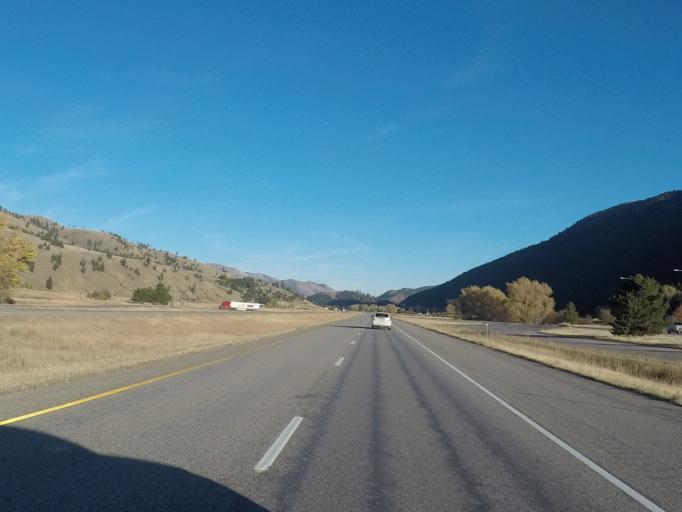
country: US
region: Montana
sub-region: Missoula County
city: Clinton
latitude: 46.7269
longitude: -113.6415
